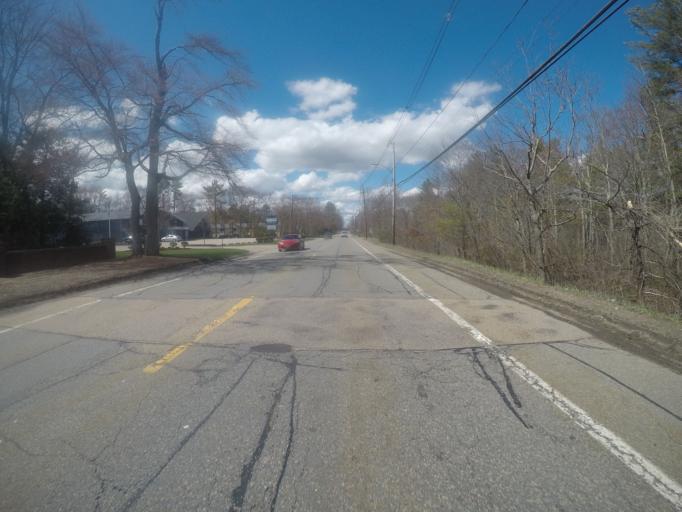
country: US
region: Massachusetts
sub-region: Bristol County
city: Easton
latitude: 42.0350
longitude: -71.0735
